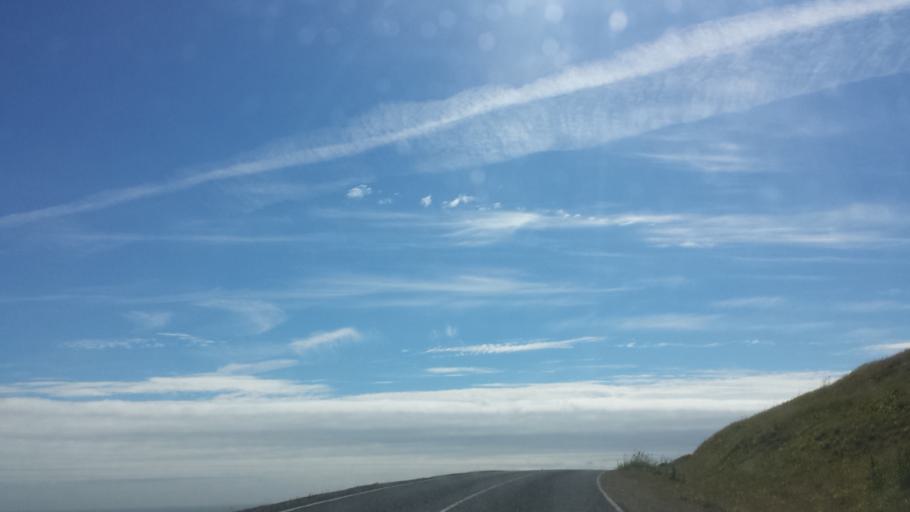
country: IS
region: South
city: Vestmannaeyjar
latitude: 63.4296
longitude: -20.2554
